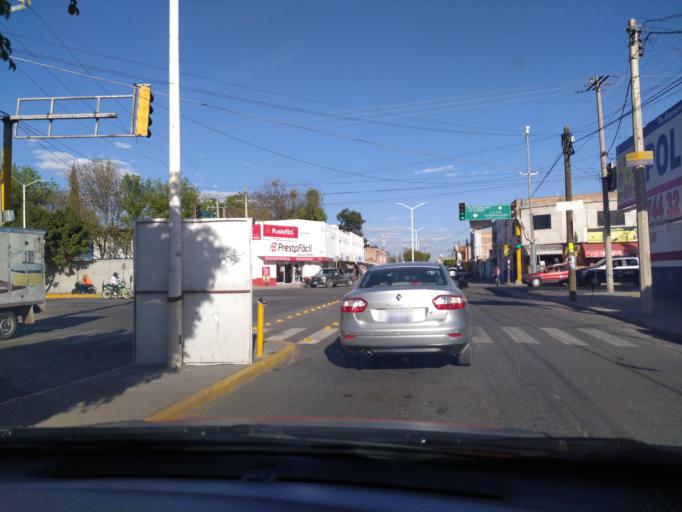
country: LA
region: Oudomxai
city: Muang La
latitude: 21.0165
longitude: 101.8504
